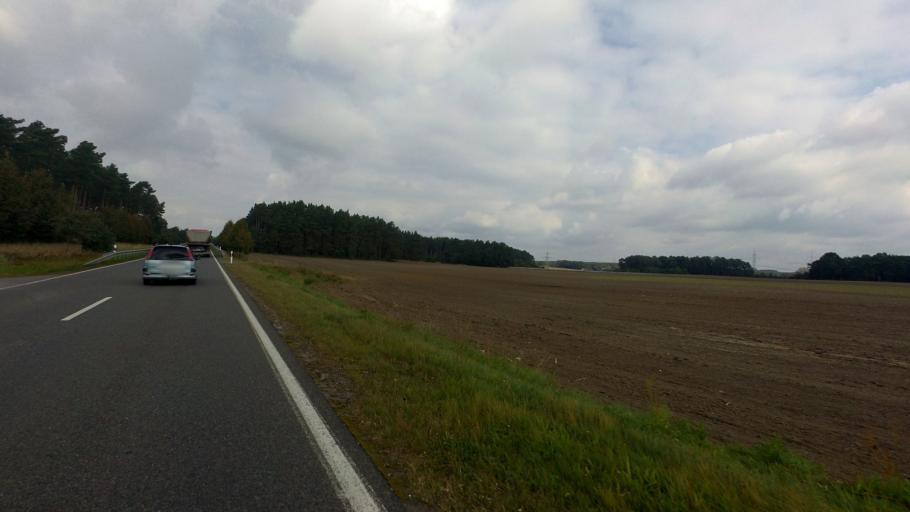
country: DE
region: Brandenburg
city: Bad Liebenwerda
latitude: 51.5282
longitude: 13.4113
